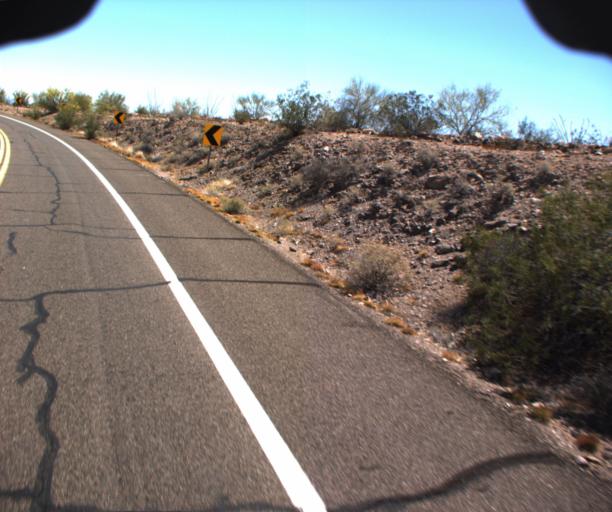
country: US
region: Arizona
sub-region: La Paz County
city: Quartzsite
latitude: 33.6600
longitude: -114.0132
